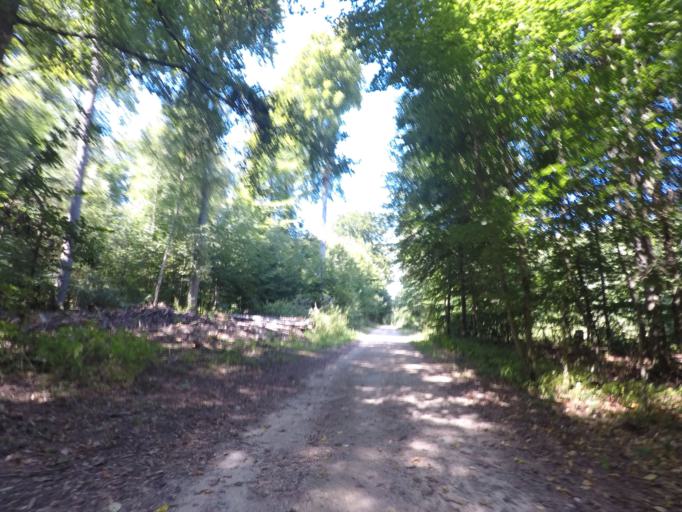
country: LU
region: Luxembourg
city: Bereldange
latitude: 49.6394
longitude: 6.1105
